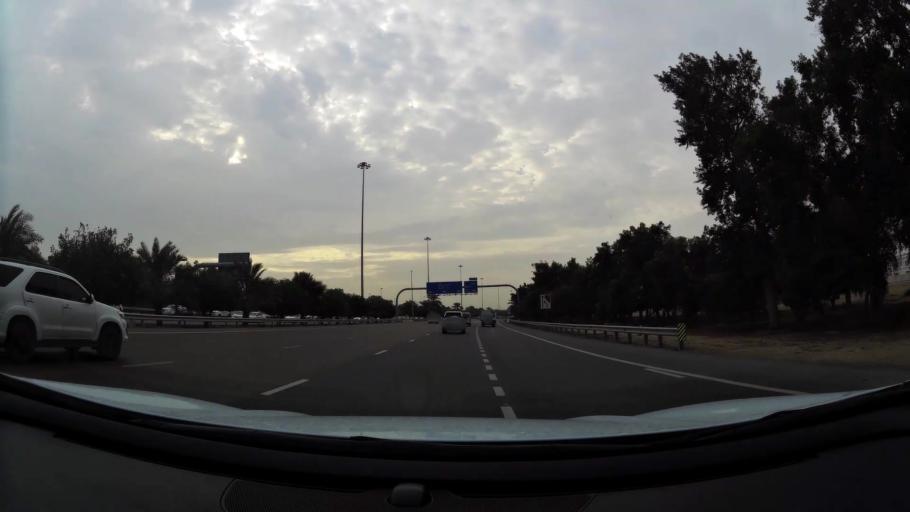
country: AE
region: Abu Dhabi
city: Abu Dhabi
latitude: 24.3630
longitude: 54.5629
